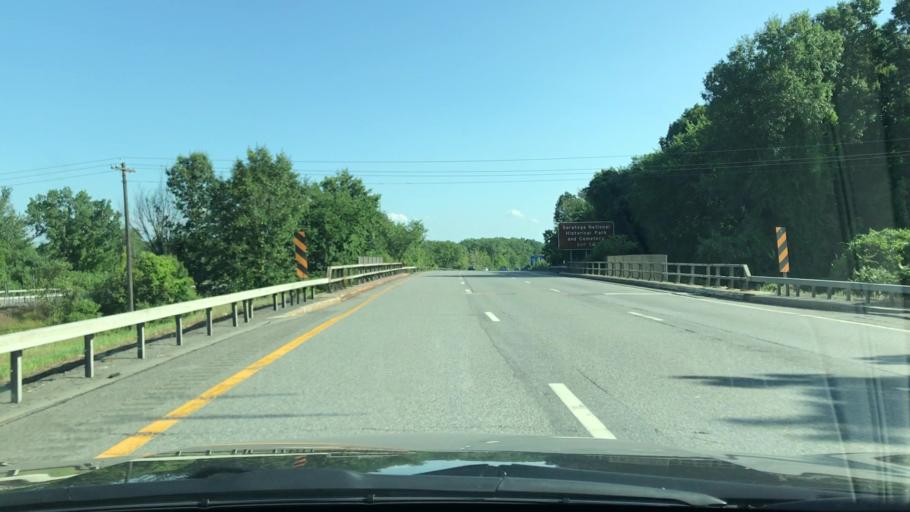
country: US
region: New York
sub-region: Saratoga County
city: Saratoga Springs
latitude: 43.0848
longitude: -73.7490
